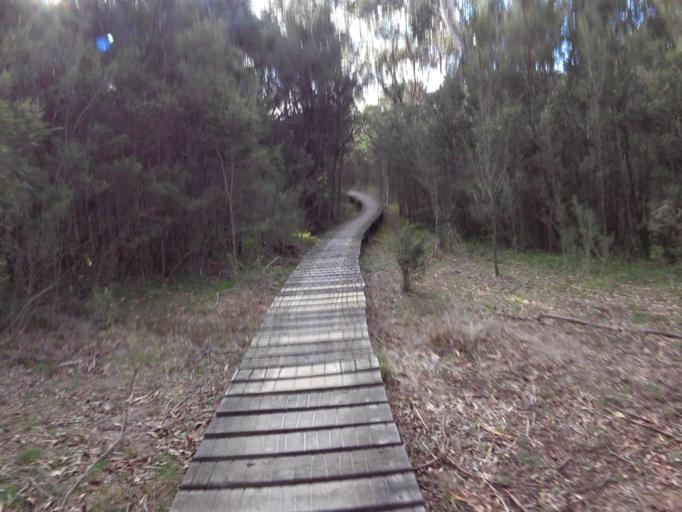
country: AU
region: Victoria
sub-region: Yarra Ranges
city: Lysterfield
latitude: -37.9442
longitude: 145.2747
